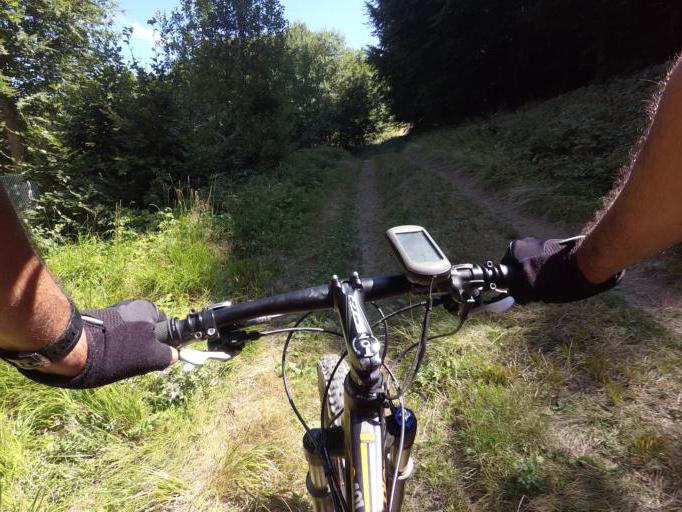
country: IT
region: Emilia-Romagna
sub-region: Provincia di Modena
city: Montecreto
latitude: 44.2148
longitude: 10.6943
